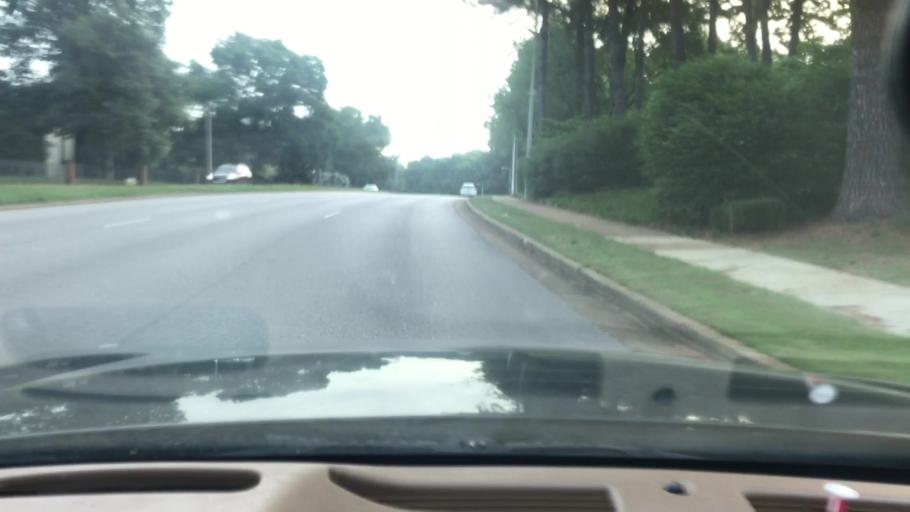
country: US
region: Tennessee
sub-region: Shelby County
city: Bartlett
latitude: 35.1844
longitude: -89.8708
